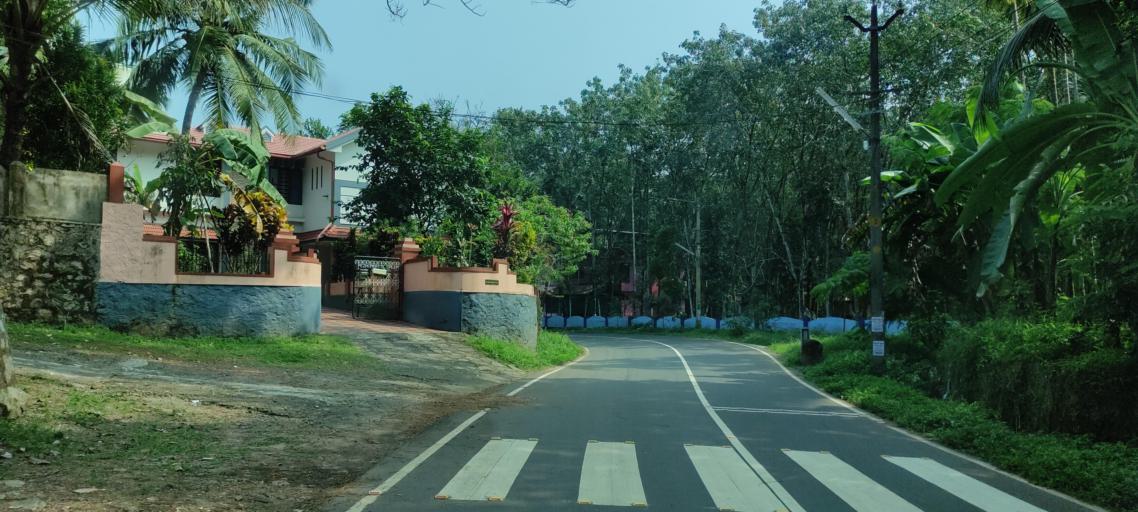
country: IN
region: Kerala
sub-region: Pattanamtitta
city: Adur
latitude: 9.2281
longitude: 76.7036
